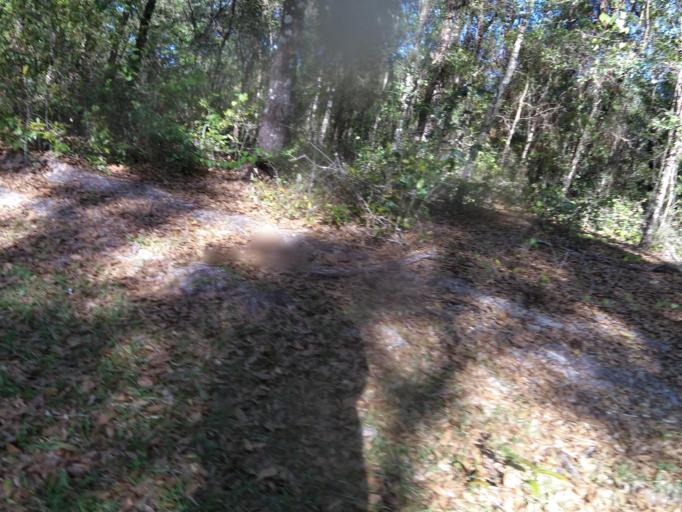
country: US
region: Florida
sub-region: Clay County
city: Keystone Heights
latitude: 29.8358
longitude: -82.0129
